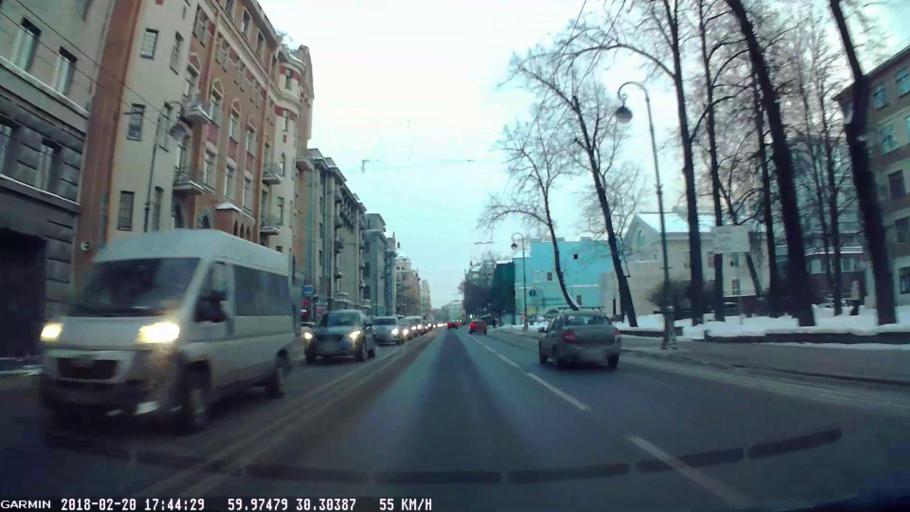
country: RU
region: St.-Petersburg
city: Petrogradka
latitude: 59.9742
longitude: 30.3043
